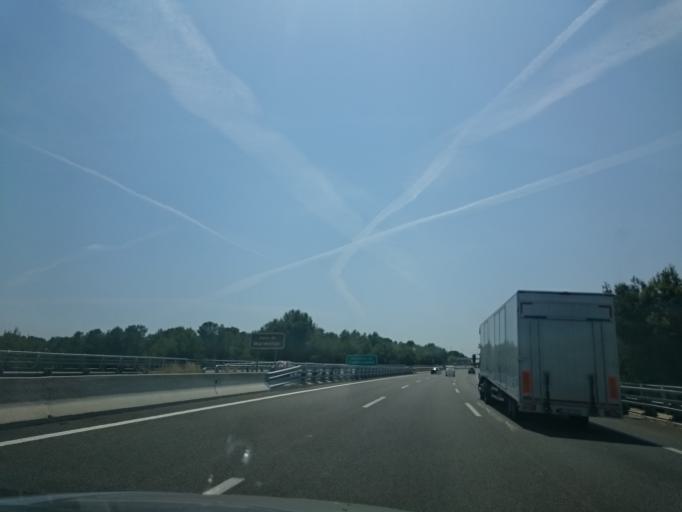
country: ES
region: Catalonia
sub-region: Provincia de Tarragona
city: Sant Jaume dels Domenys
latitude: 41.2923
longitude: 1.5971
